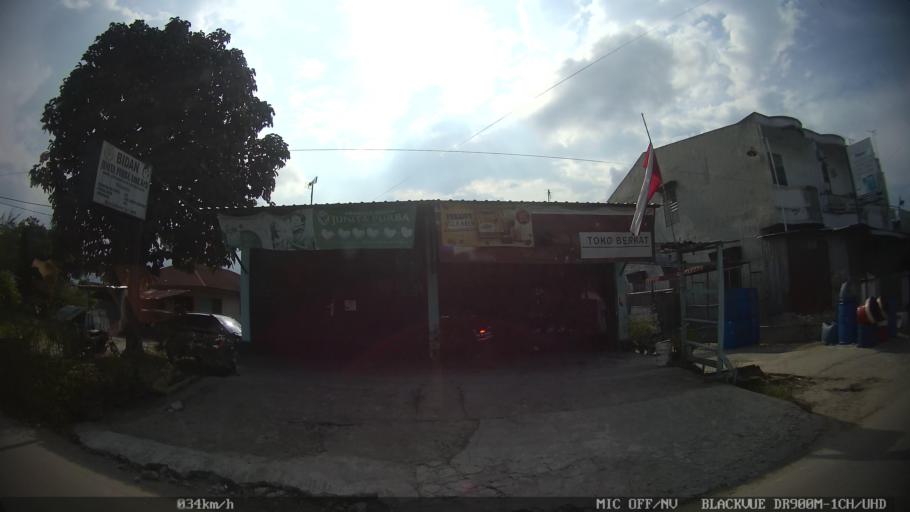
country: ID
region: North Sumatra
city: Medan
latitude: 3.5791
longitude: 98.7566
